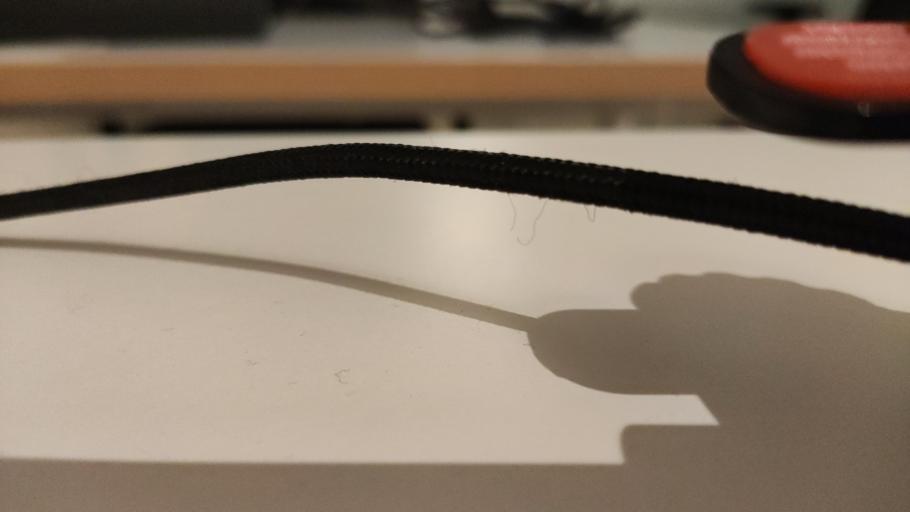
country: RU
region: Moskovskaya
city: Kurovskoye
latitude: 55.5828
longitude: 38.8900
